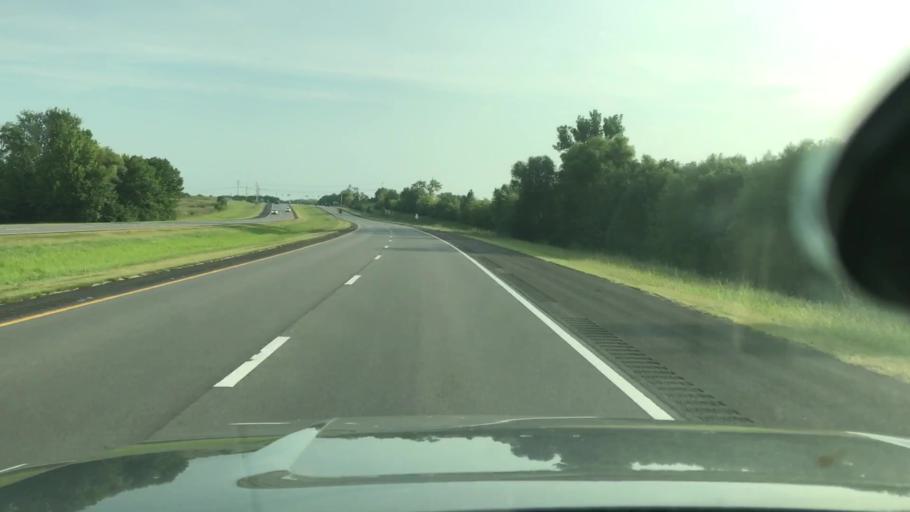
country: US
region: Tennessee
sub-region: Sumner County
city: Gallatin
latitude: 36.4032
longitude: -86.4778
